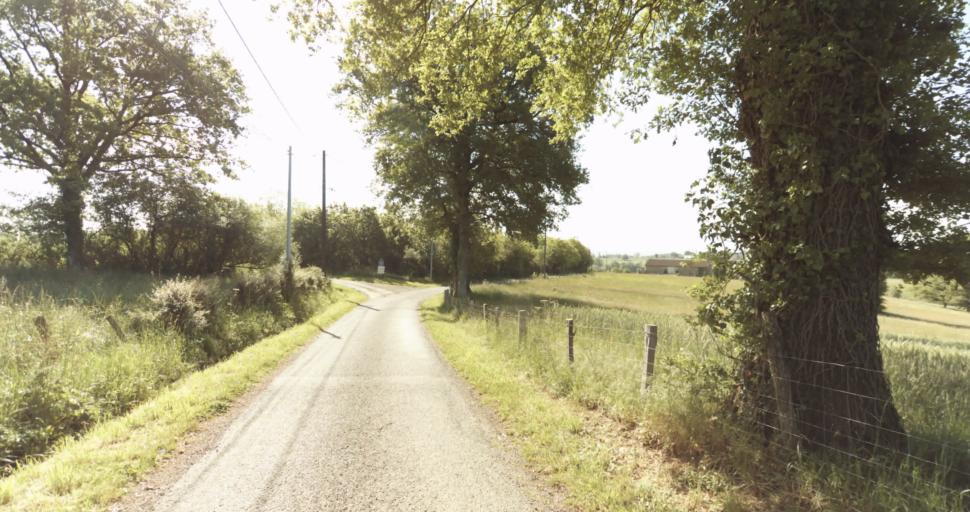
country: FR
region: Limousin
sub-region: Departement de la Haute-Vienne
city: Solignac
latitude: 45.7127
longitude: 1.2665
